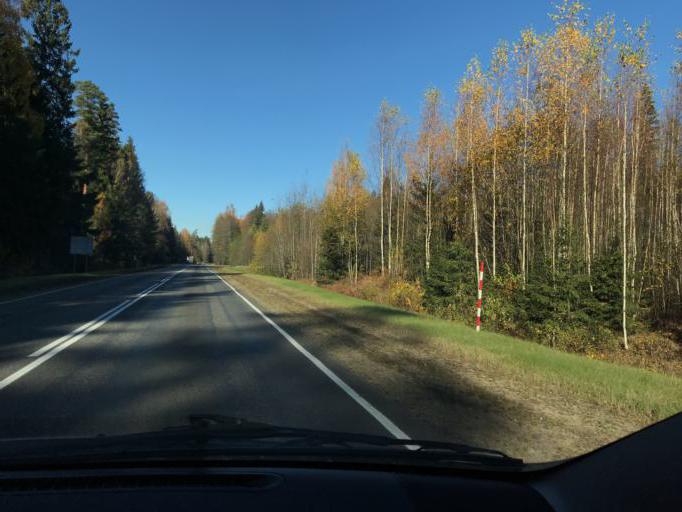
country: BY
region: Vitebsk
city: Polatsk
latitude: 55.4155
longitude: 28.7954
